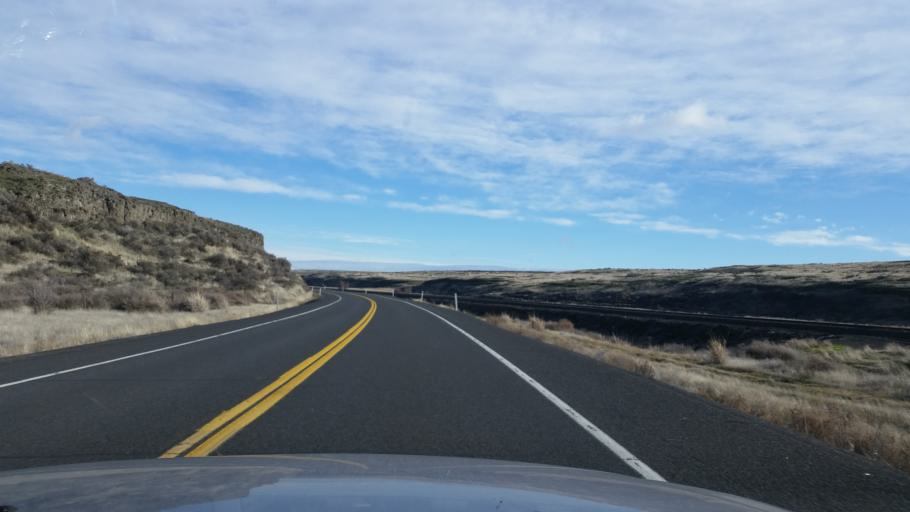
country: US
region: Washington
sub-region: Adams County
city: Ritzville
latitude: 47.3572
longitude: -118.5017
